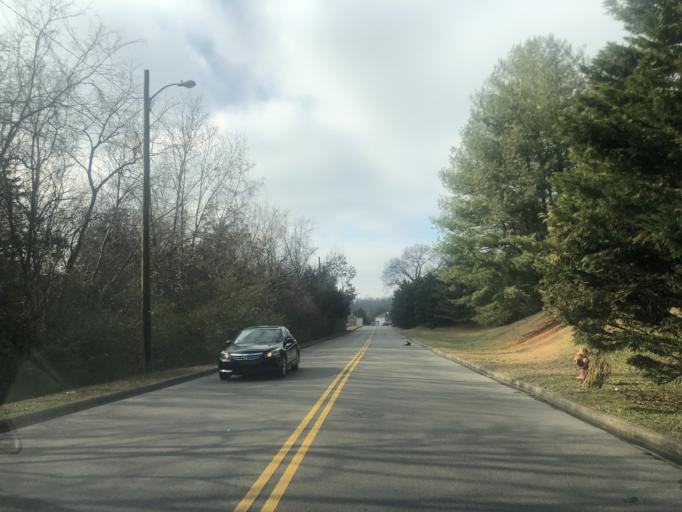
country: US
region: Tennessee
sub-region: Rutherford County
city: La Vergne
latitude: 36.0761
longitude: -86.6447
